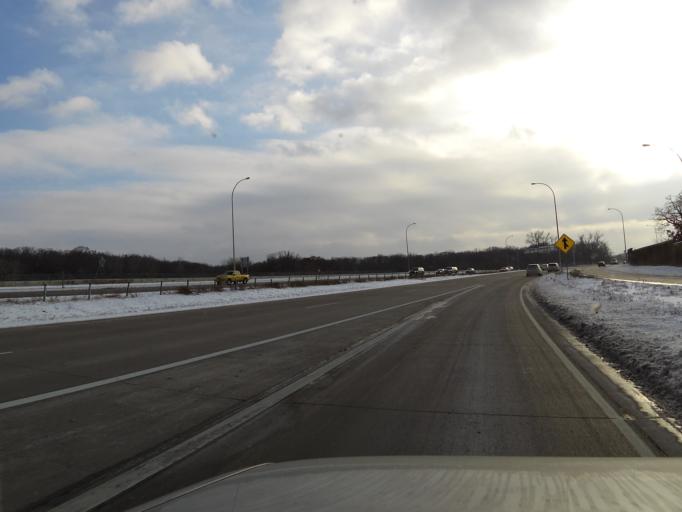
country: US
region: Minnesota
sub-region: Hennepin County
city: Edina
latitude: 44.8553
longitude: -93.3942
